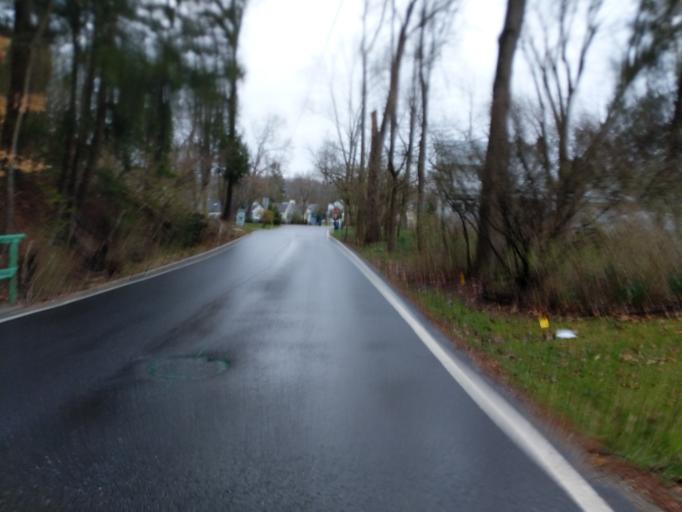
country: US
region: Ohio
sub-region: Athens County
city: Athens
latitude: 39.3406
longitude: -82.0885
